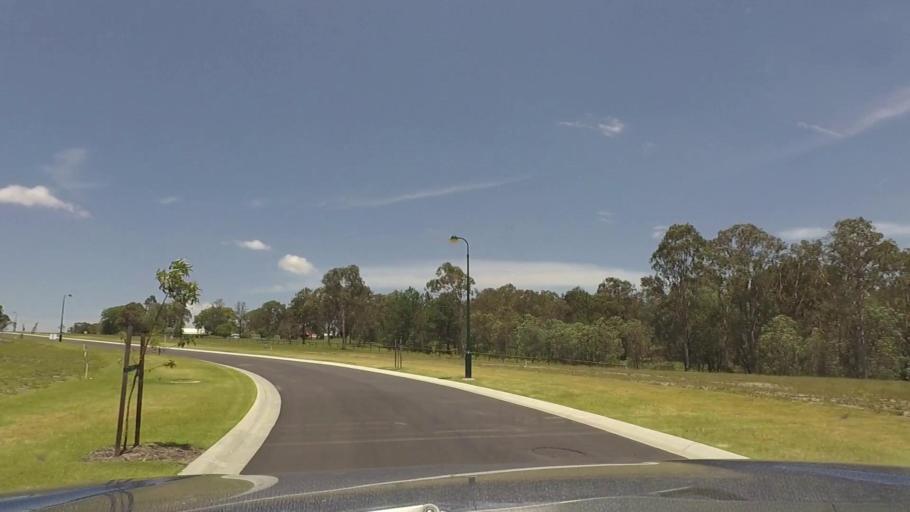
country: AU
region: Queensland
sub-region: Logan
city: Chambers Flat
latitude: -27.7733
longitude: 153.0873
